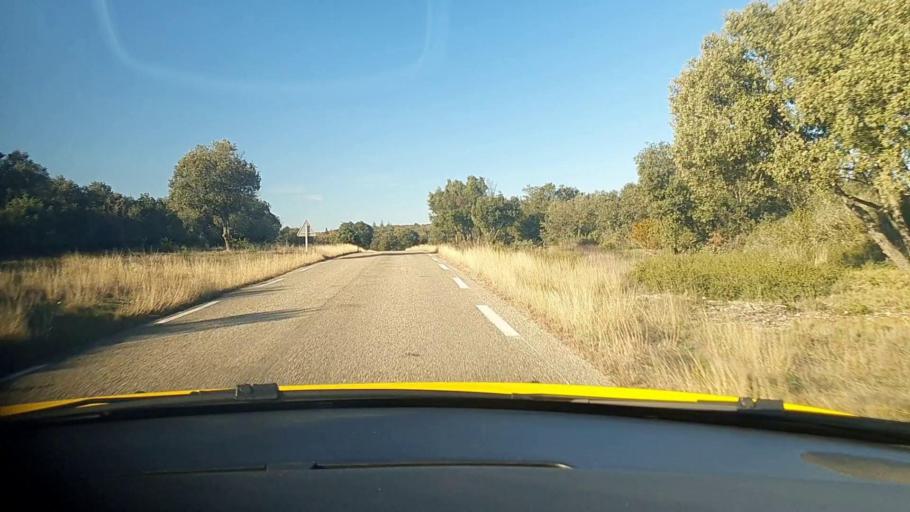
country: FR
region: Languedoc-Roussillon
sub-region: Departement du Gard
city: Goudargues
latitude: 44.1622
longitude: 4.3441
